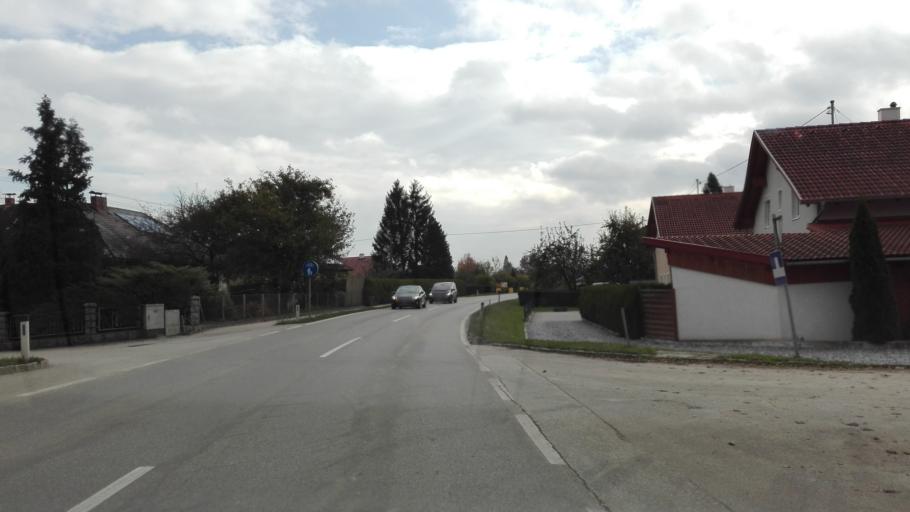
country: AT
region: Upper Austria
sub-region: Politischer Bezirk Urfahr-Umgebung
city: Feldkirchen an der Donau
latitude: 48.3291
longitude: 14.0093
